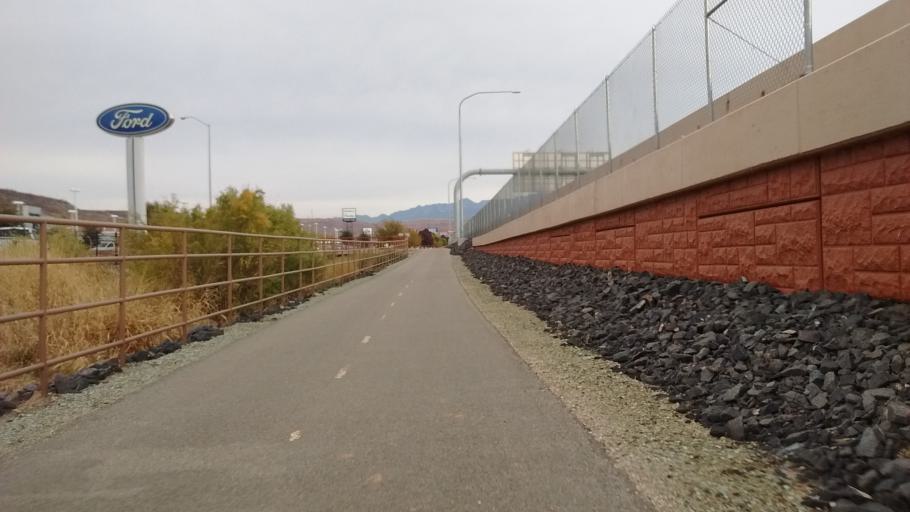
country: US
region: Utah
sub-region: Washington County
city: Saint George
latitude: 37.0770
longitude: -113.5855
